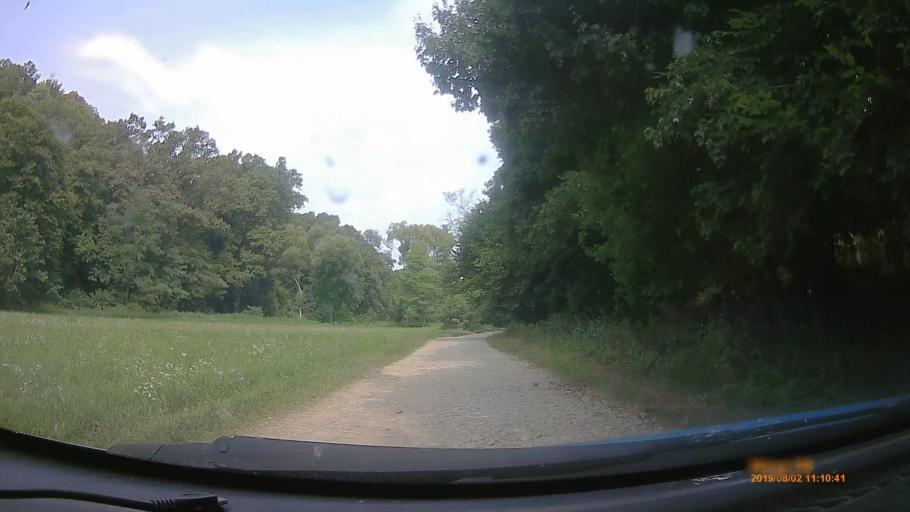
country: HU
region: Baranya
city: Buekkoesd
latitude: 46.1052
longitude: 17.9369
